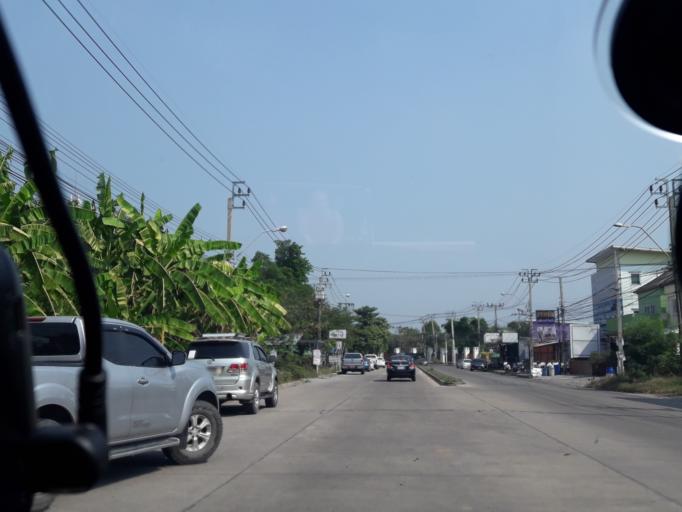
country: TH
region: Bangkok
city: Khlong Sam Wa
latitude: 13.8530
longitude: 100.7056
